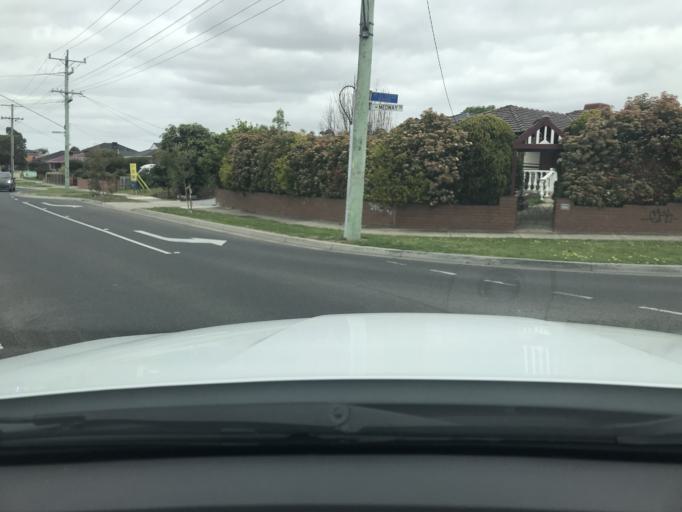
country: AU
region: Victoria
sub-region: Hume
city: Craigieburn
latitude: -37.5921
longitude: 144.9372
